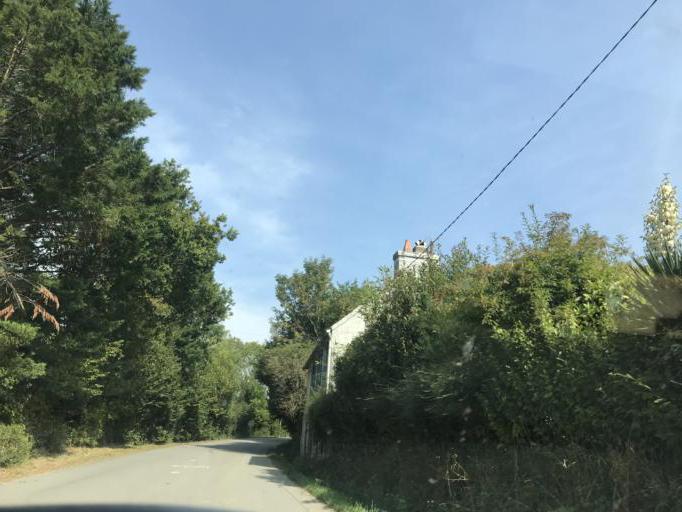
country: FR
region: Brittany
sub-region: Departement du Finistere
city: Loperec
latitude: 48.3008
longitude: -4.0325
